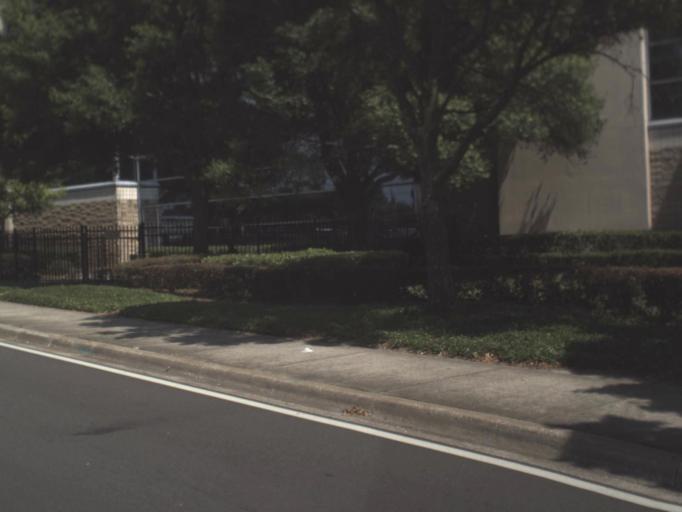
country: US
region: Florida
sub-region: Duval County
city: Jacksonville
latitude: 30.3466
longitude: -81.6632
